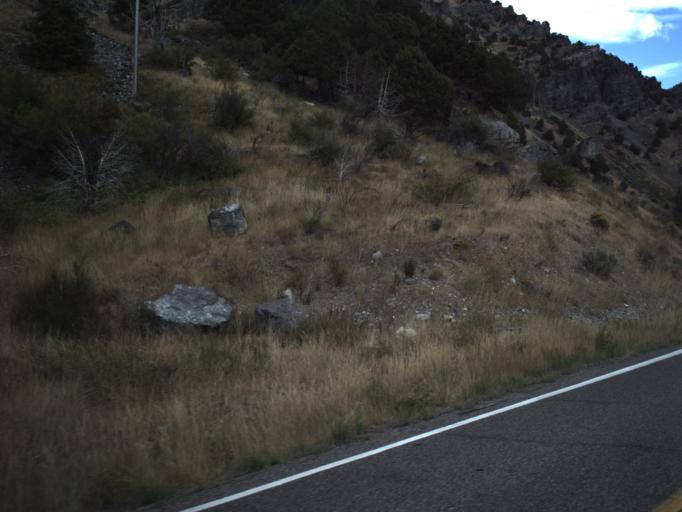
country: US
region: Utah
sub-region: Cache County
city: Hyrum
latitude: 41.6249
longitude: -111.7896
